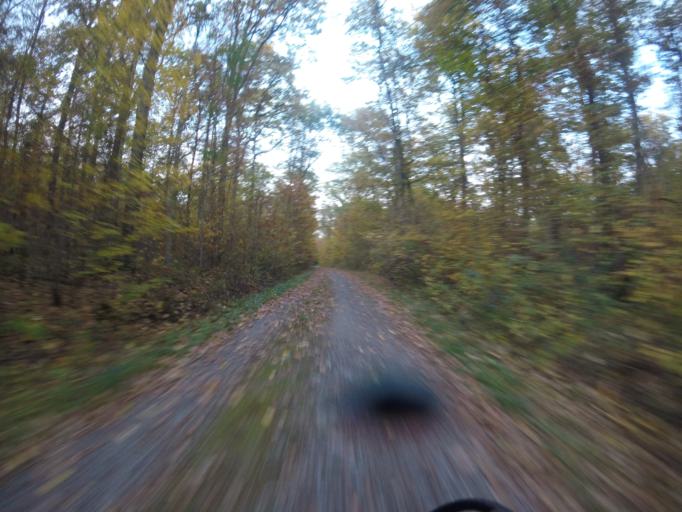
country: DE
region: Baden-Wuerttemberg
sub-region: Regierungsbezirk Stuttgart
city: Oberstenfeld
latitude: 48.9902
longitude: 9.3430
